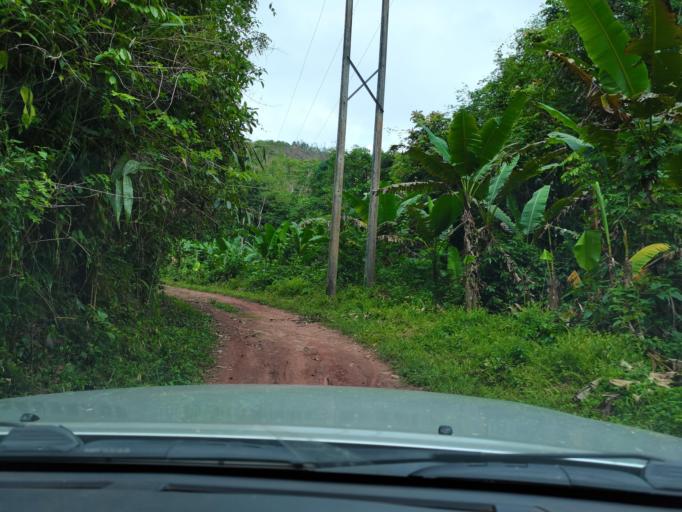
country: LA
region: Loungnamtha
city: Muang Nale
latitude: 20.5156
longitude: 101.0738
